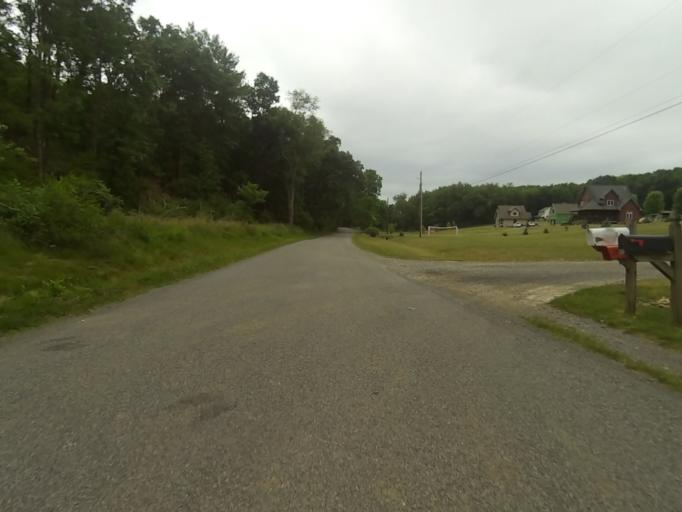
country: US
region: Pennsylvania
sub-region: Centre County
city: Stormstown
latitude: 40.7017
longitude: -78.0928
